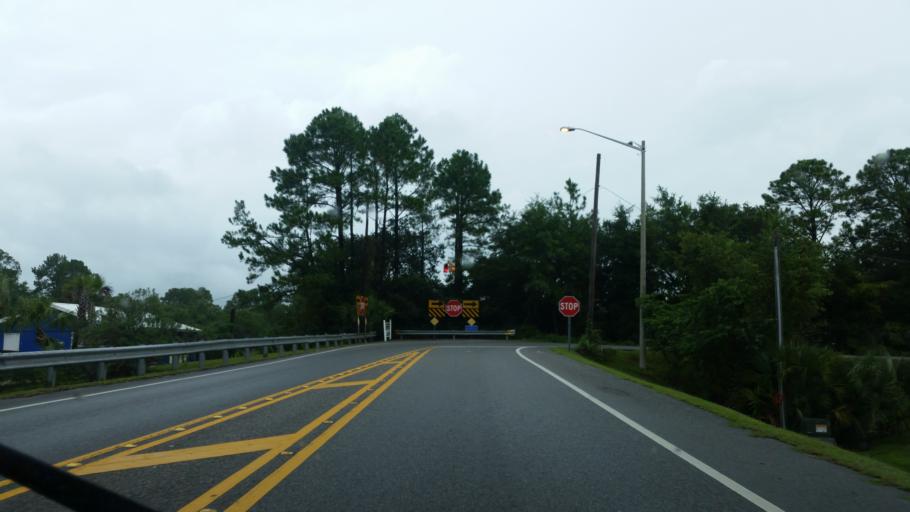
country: US
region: Alabama
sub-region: Baldwin County
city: Gulf Shores
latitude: 30.2786
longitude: -87.6831
